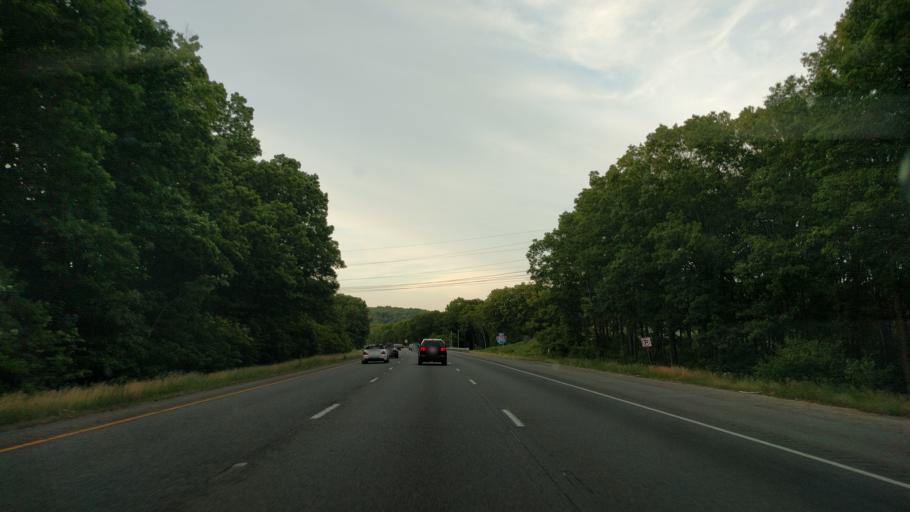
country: US
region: Massachusetts
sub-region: Worcester County
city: Shrewsbury
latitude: 42.2981
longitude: -71.7423
